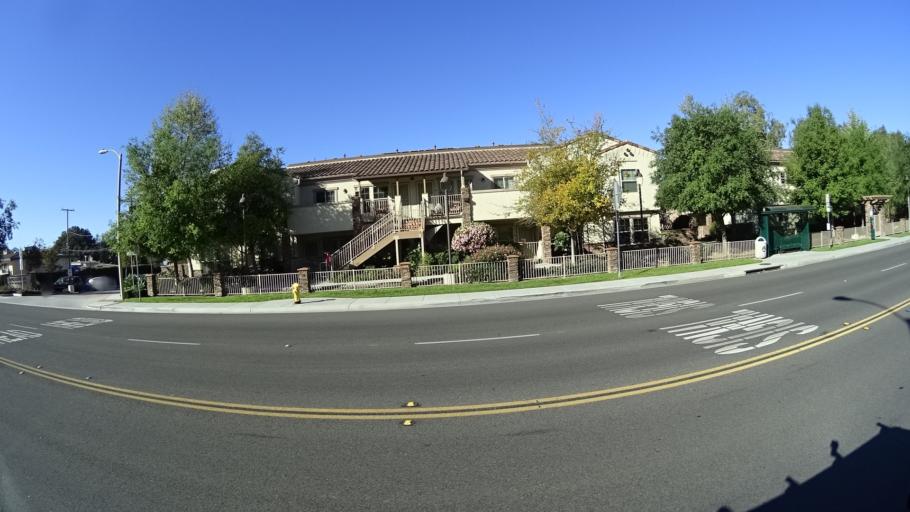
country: US
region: California
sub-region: Ventura County
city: Thousand Oaks
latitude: 34.1748
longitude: -118.8369
